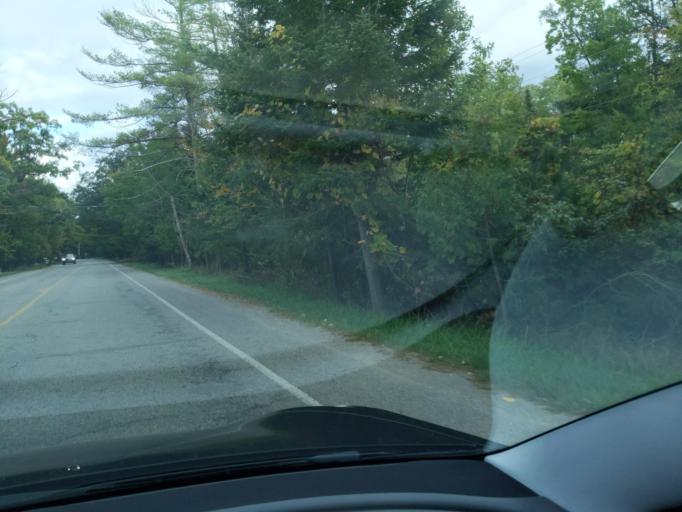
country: US
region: Michigan
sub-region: Kalkaska County
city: Rapid City
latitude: 44.8517
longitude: -85.3201
